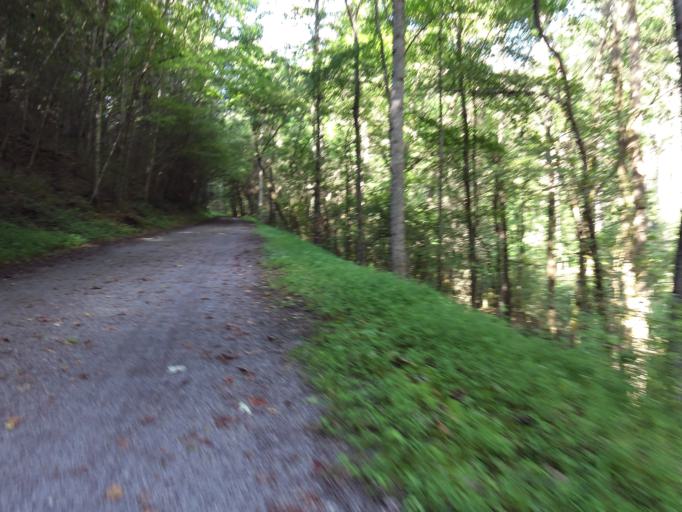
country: US
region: Virginia
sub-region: Washington County
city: Abingdon
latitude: 36.6881
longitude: -81.9397
